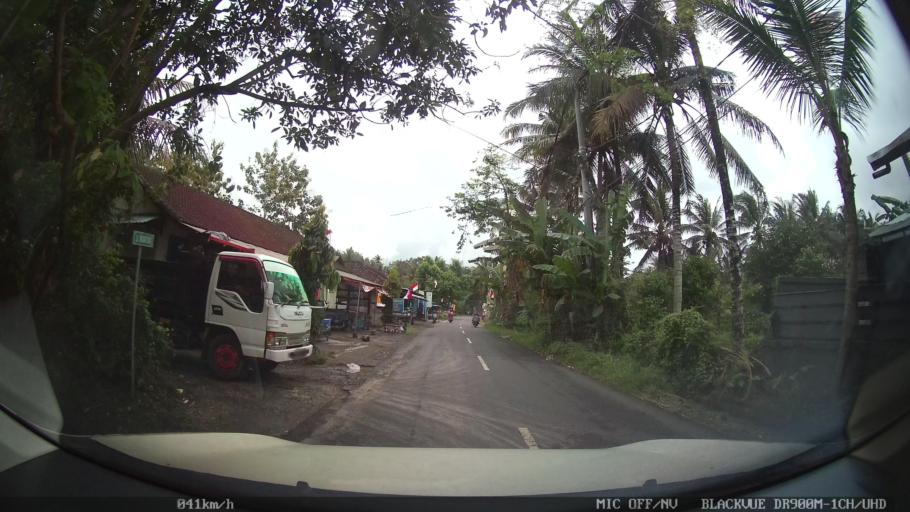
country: ID
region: Bali
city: Banjar Parekan
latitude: -8.5753
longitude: 115.2114
